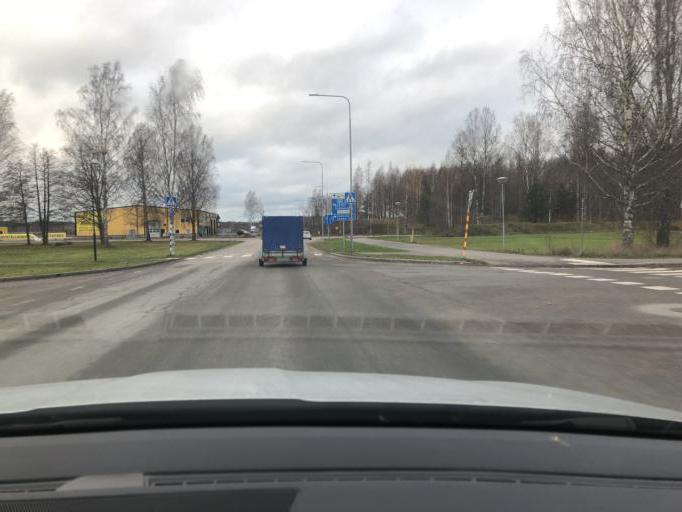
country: SE
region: Uppsala
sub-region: Tierps Kommun
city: Tierp
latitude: 60.3478
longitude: 17.4994
